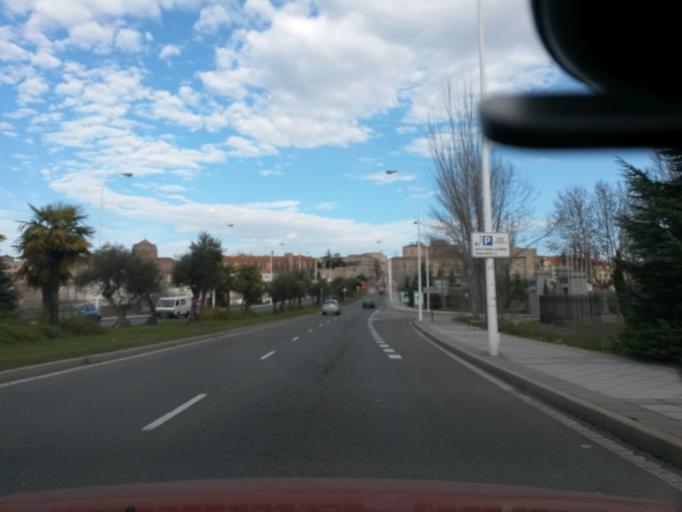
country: ES
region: Castille and Leon
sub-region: Provincia de Salamanca
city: Salamanca
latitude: 40.9556
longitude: -5.6615
